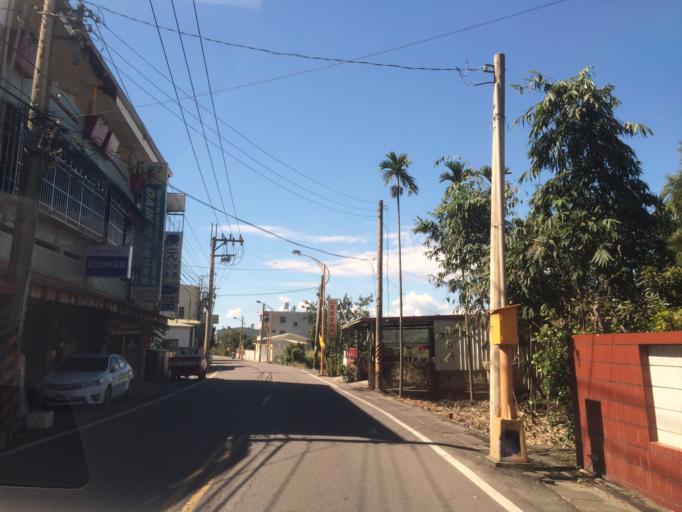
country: TW
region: Taiwan
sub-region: Yunlin
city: Douliu
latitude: 23.7032
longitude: 120.5962
